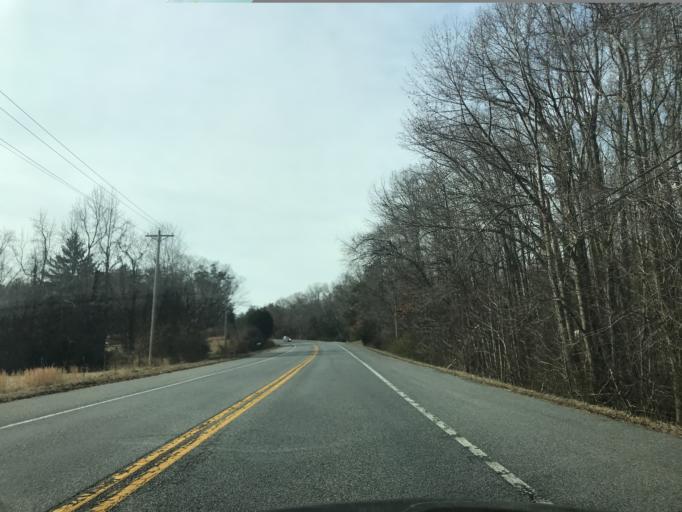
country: US
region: Maryland
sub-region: Charles County
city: La Plata
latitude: 38.4994
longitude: -77.0630
